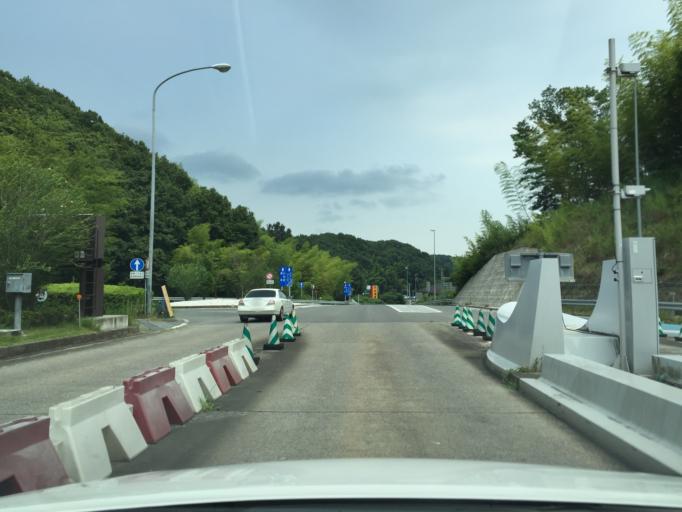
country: JP
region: Fukushima
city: Iwaki
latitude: 37.0017
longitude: 140.8130
